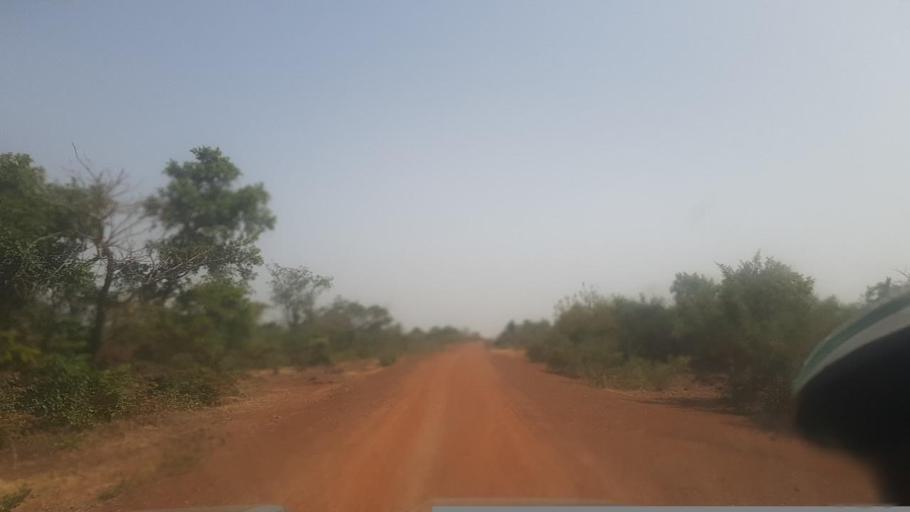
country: ML
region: Segou
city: Segou
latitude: 12.9288
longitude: -6.2775
